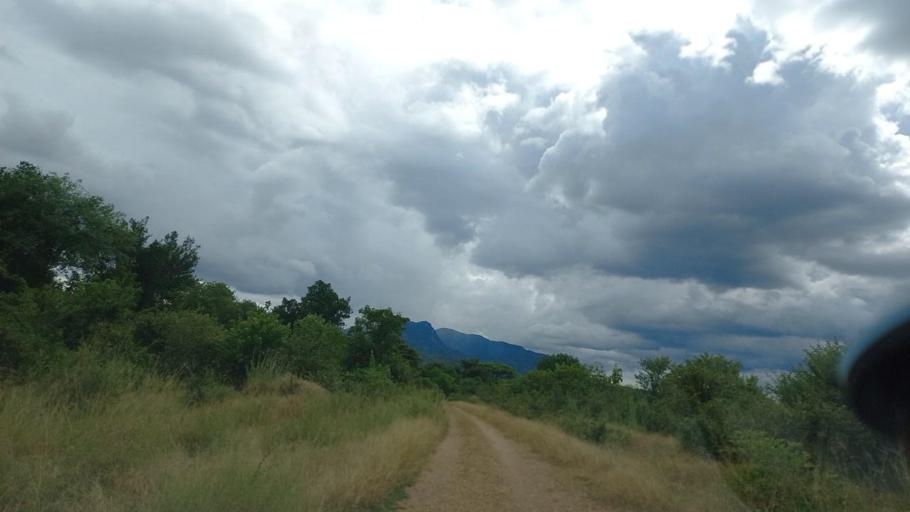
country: ZM
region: Lusaka
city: Luangwa
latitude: -15.6521
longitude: 30.3512
